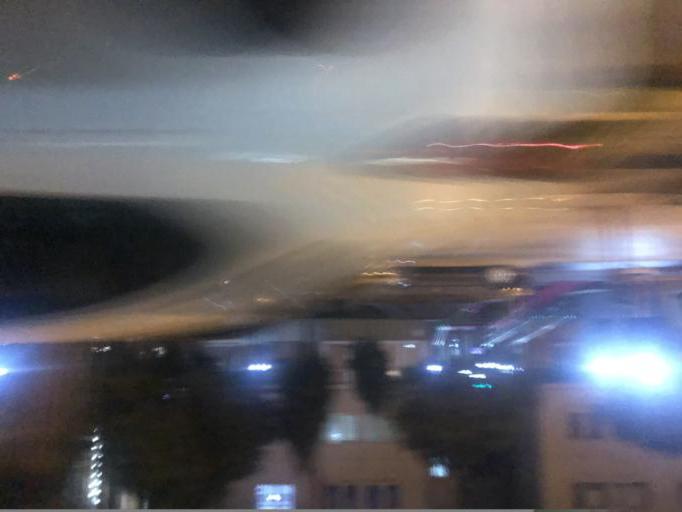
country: TR
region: Istanbul
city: Bahcelievler
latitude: 40.9777
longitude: 28.8558
